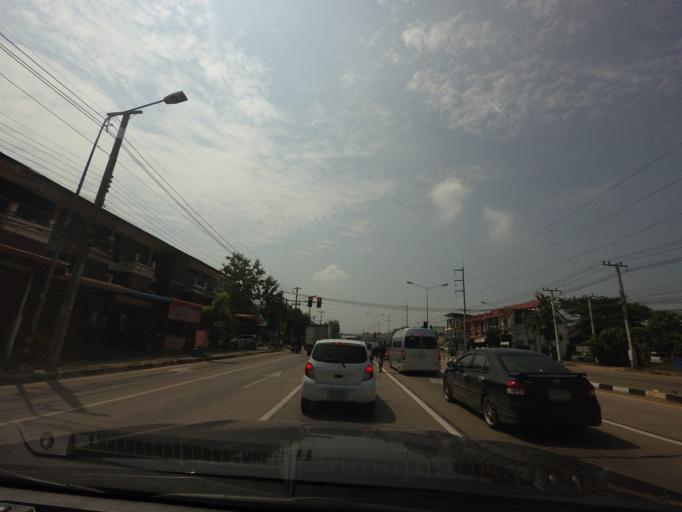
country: TH
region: Phrae
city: Sung Men
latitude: 18.0742
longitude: 100.1216
